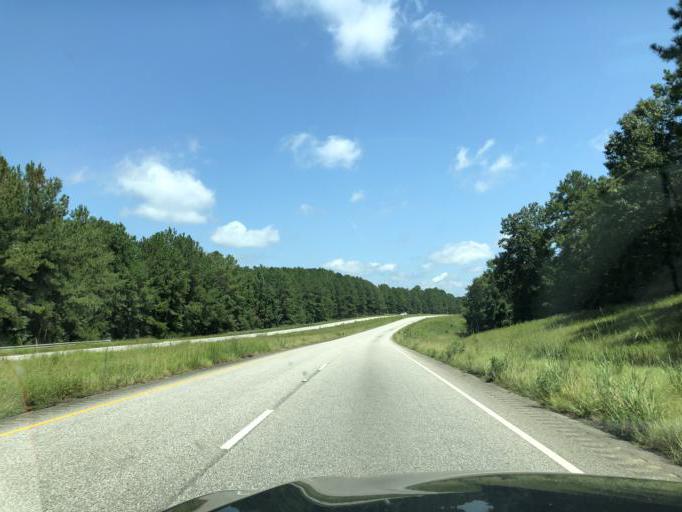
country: US
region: Alabama
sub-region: Henry County
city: Abbeville
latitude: 31.7355
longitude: -85.2522
